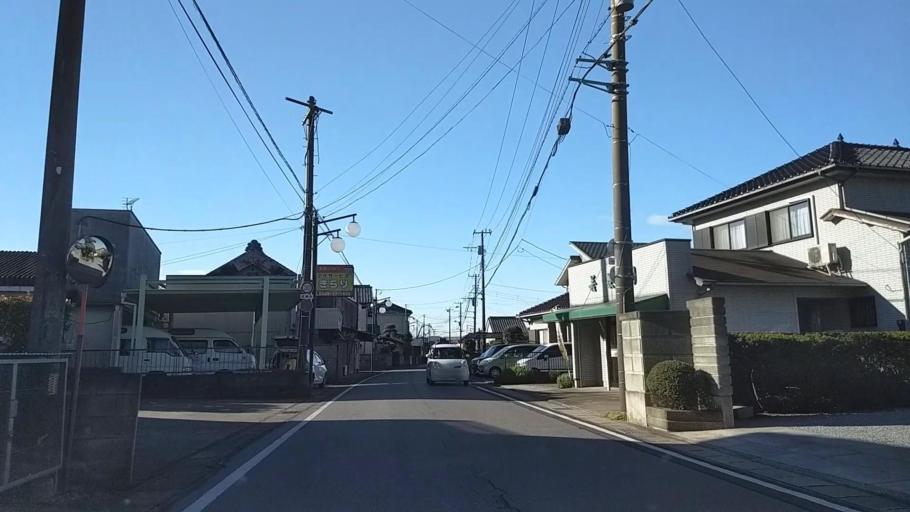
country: JP
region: Chiba
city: Futtsu
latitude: 35.2831
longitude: 139.8566
